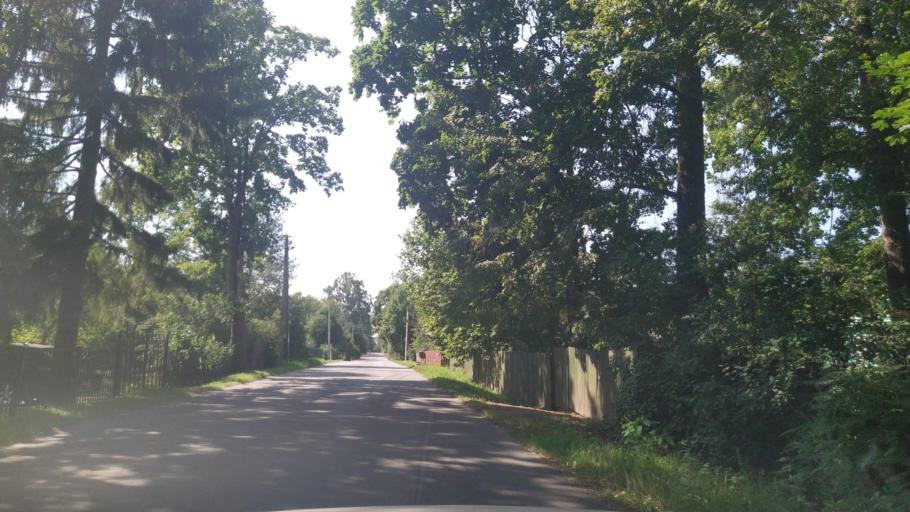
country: RU
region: Leningrad
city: Siverskiy
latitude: 59.2778
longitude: 30.0493
